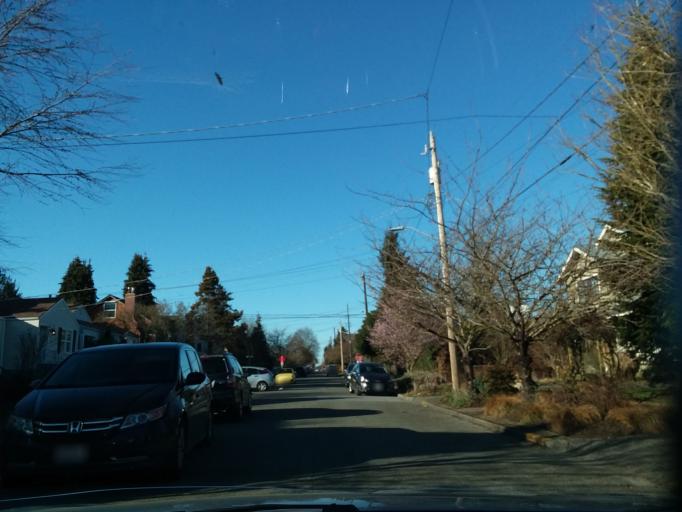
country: US
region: Washington
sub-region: King County
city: Shoreline
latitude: 47.6863
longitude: -122.3673
